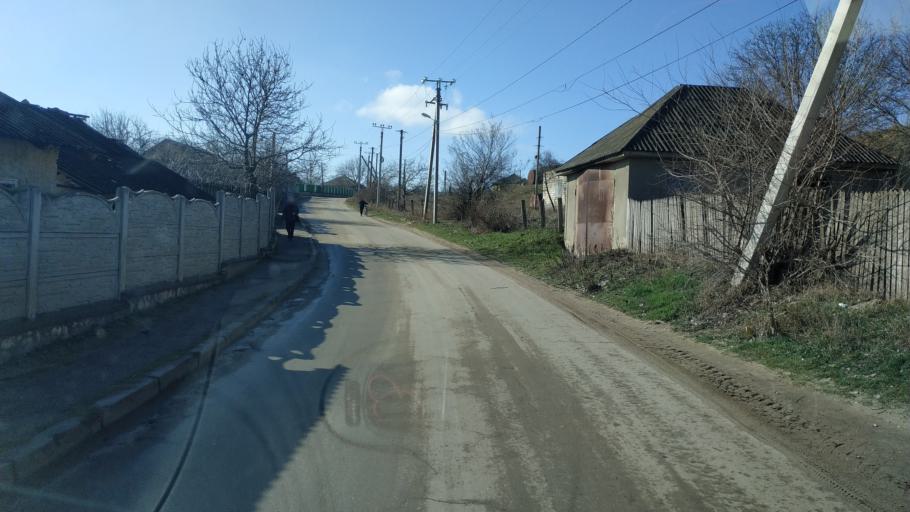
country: MD
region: Hincesti
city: Hincesti
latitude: 46.9350
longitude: 28.6387
